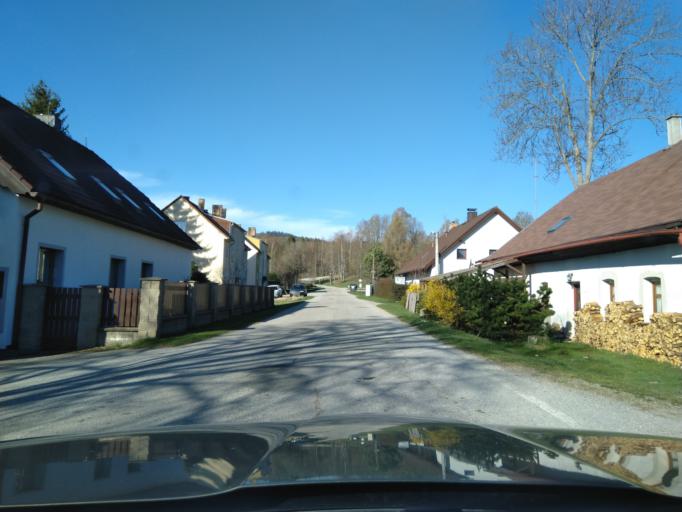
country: CZ
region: Jihocesky
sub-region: Okres Cesky Krumlov
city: Horni Plana
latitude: 48.7784
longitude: 13.9340
